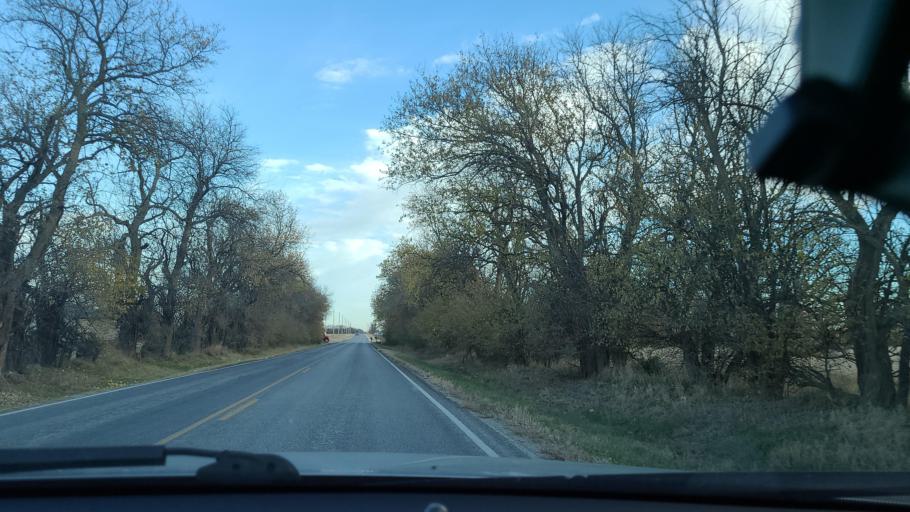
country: US
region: Kansas
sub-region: Sedgwick County
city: Goddard
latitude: 37.6498
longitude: -97.5458
